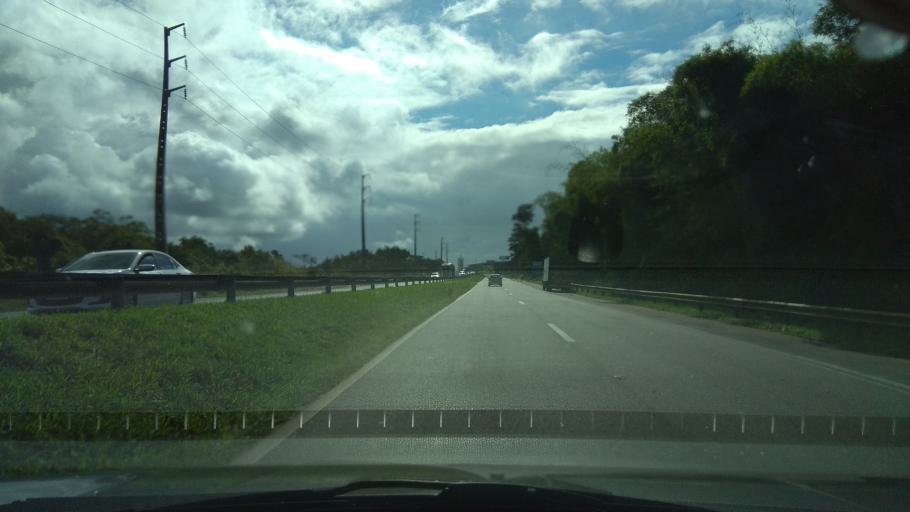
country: BR
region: Bahia
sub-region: Conceicao Do Jacuipe
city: Conceicao do Jacuipe
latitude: -12.3480
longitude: -38.8363
